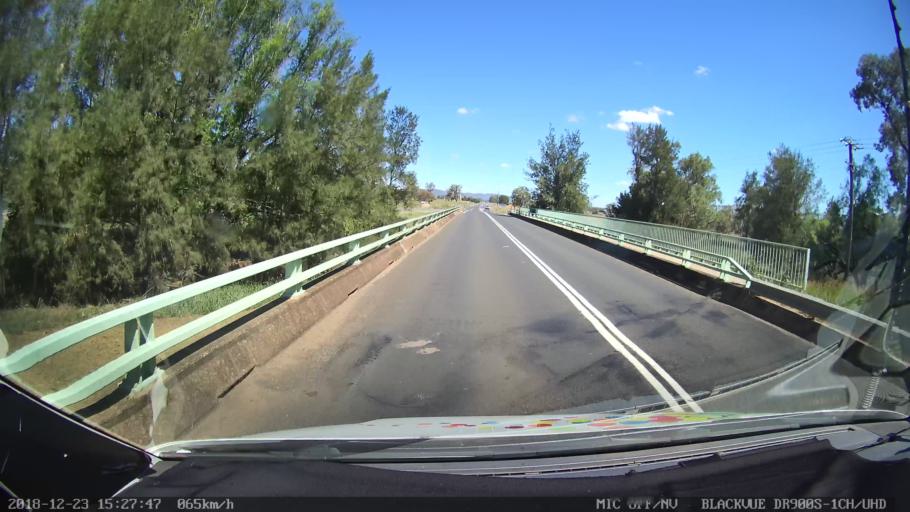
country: AU
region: New South Wales
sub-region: Tamworth Municipality
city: East Tamworth
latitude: -30.9304
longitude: 150.8476
